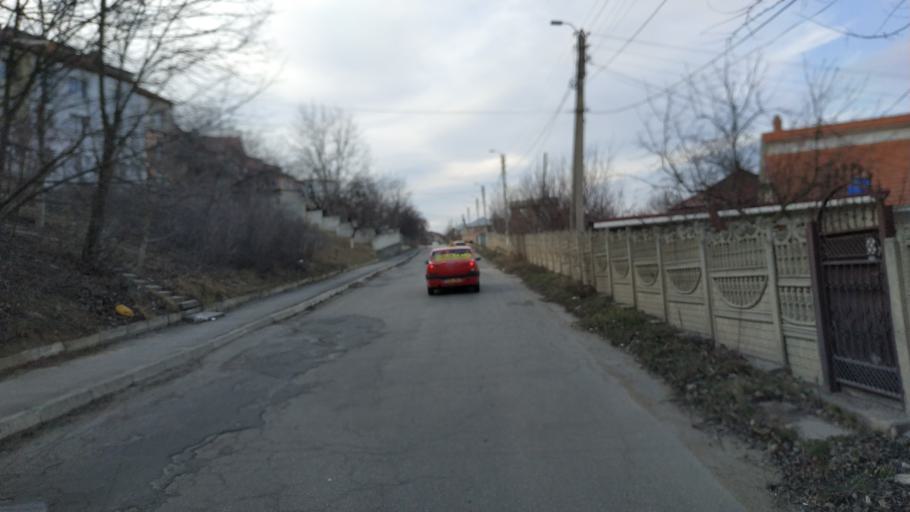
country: MD
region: Laloveni
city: Ialoveni
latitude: 46.9545
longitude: 28.7628
